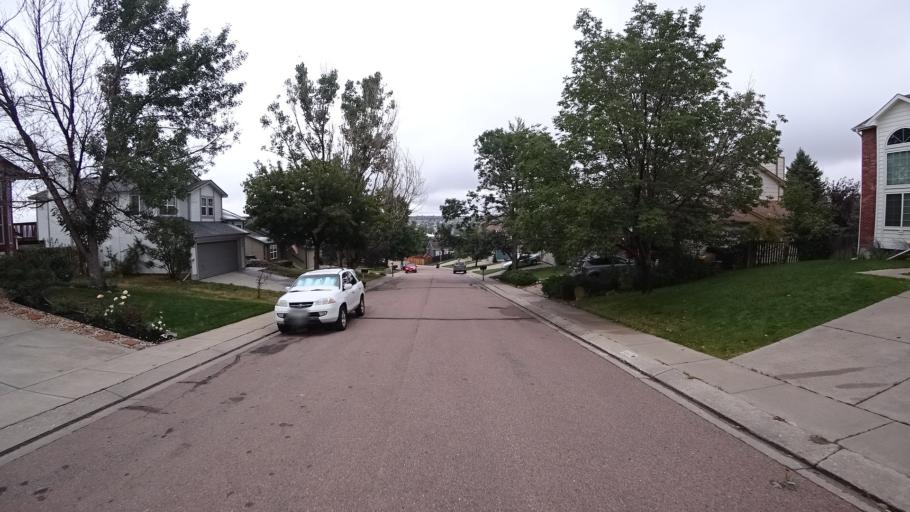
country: US
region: Colorado
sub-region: El Paso County
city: Cimarron Hills
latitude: 38.9234
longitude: -104.7571
